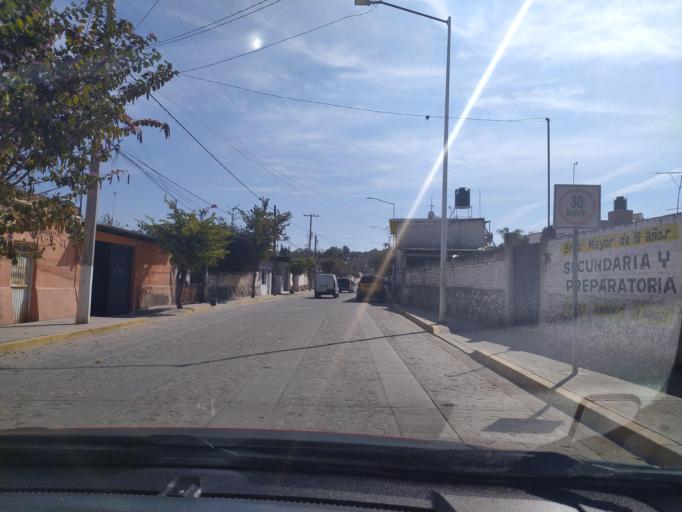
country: MX
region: Guanajuato
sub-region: San Francisco del Rincon
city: San Ignacio de Hidalgo
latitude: 20.8809
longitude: -101.8553
